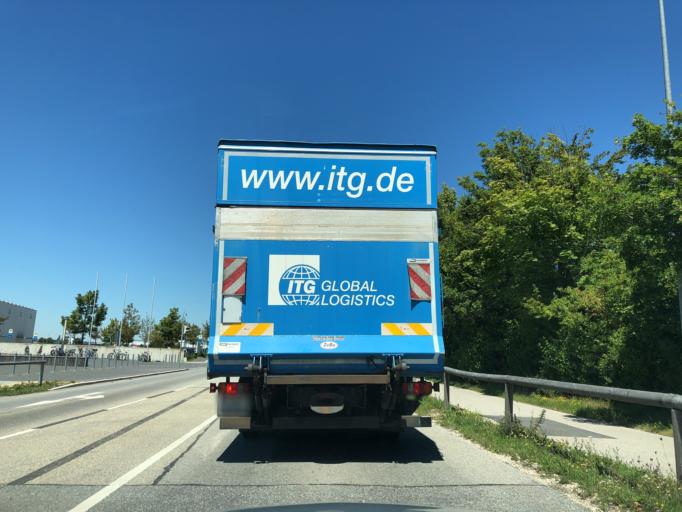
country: DE
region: Bavaria
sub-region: Upper Bavaria
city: Erding
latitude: 48.2972
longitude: 11.8920
